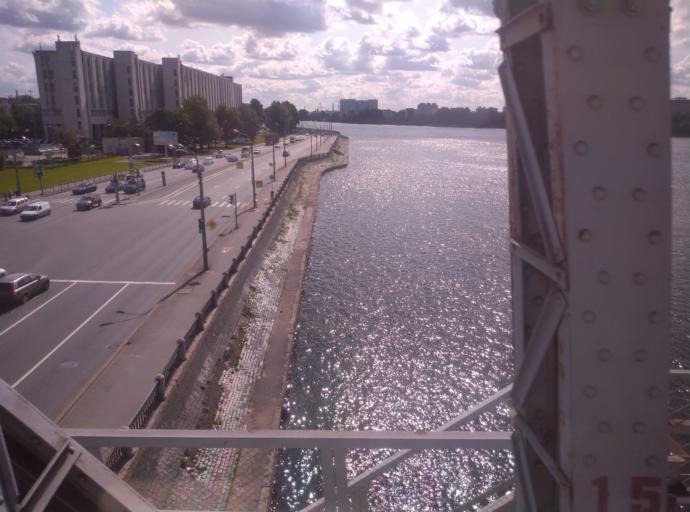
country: RU
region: St.-Petersburg
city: Centralniy
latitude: 59.9162
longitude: 30.4131
